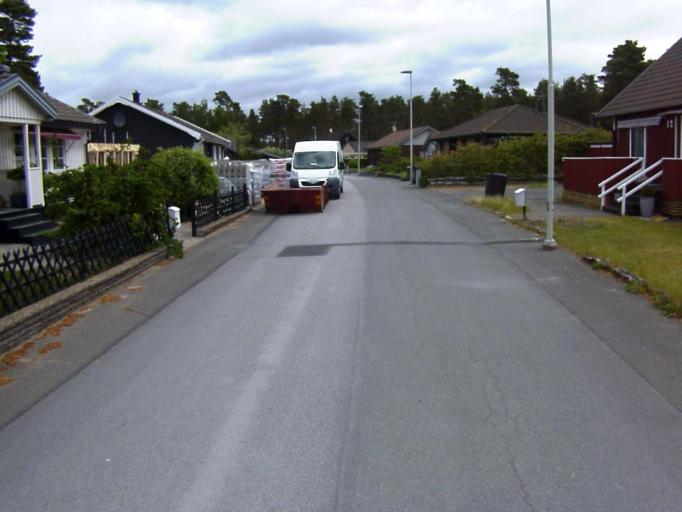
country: SE
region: Skane
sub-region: Kristianstads Kommun
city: Ahus
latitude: 55.9414
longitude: 14.2773
